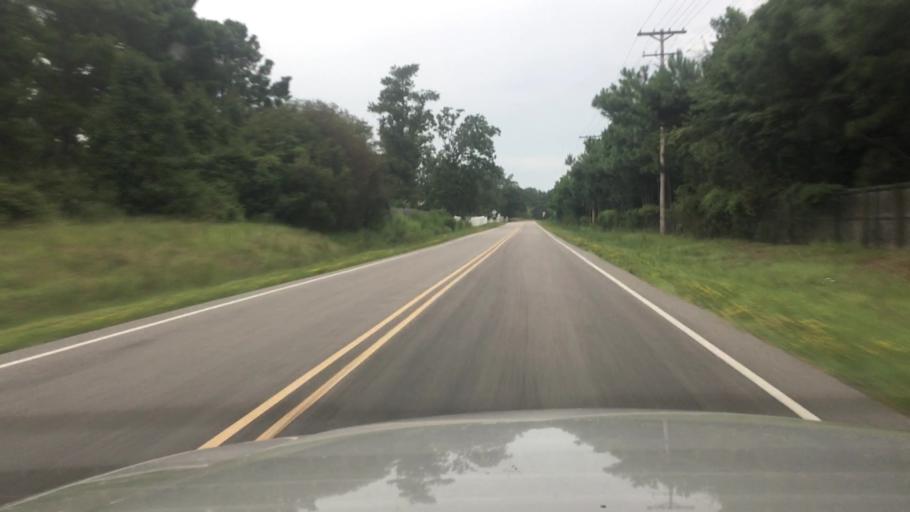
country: US
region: North Carolina
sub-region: Hoke County
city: Rockfish
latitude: 34.9931
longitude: -79.0235
